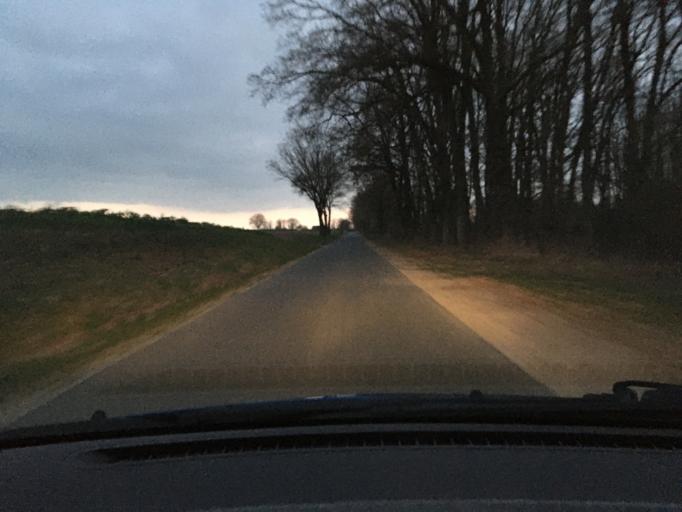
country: DE
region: Lower Saxony
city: Thomasburg
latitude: 53.2323
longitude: 10.6322
